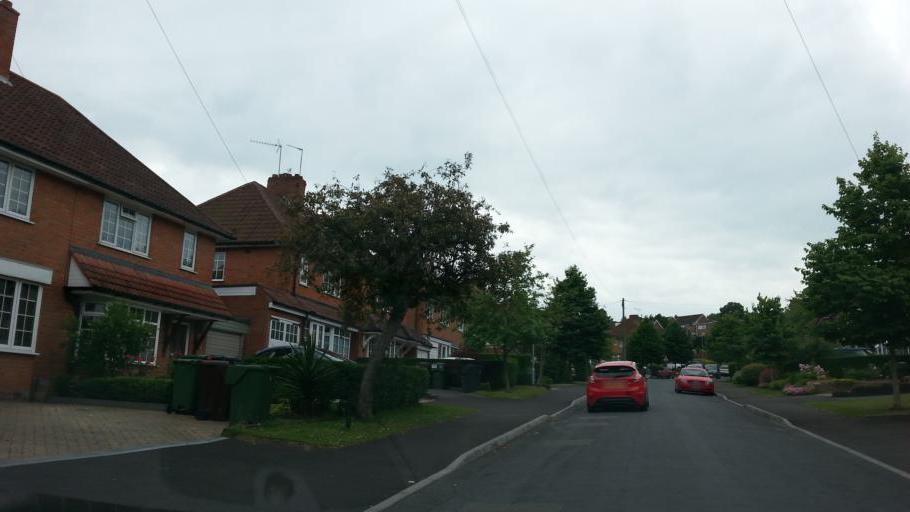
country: GB
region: England
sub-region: Worcestershire
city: Barnt Green
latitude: 52.3908
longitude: -2.0223
